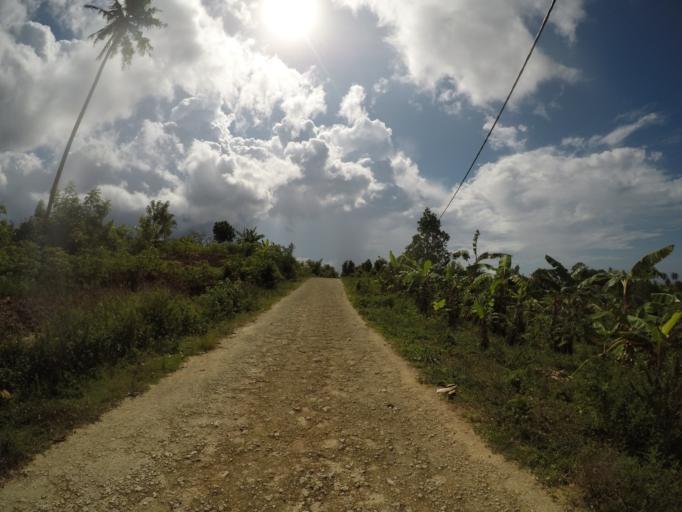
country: TZ
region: Pemba South
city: Mtambile
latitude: -5.3487
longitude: 39.6926
